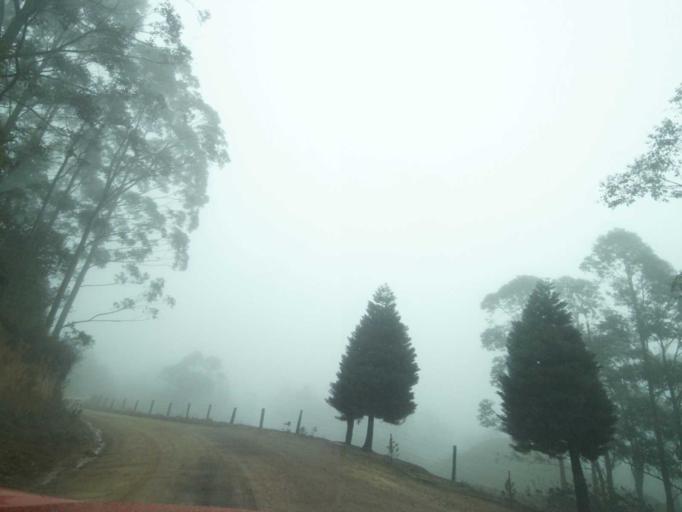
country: BR
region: Santa Catarina
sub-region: Anitapolis
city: Anitapolis
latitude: -27.9201
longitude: -49.1785
